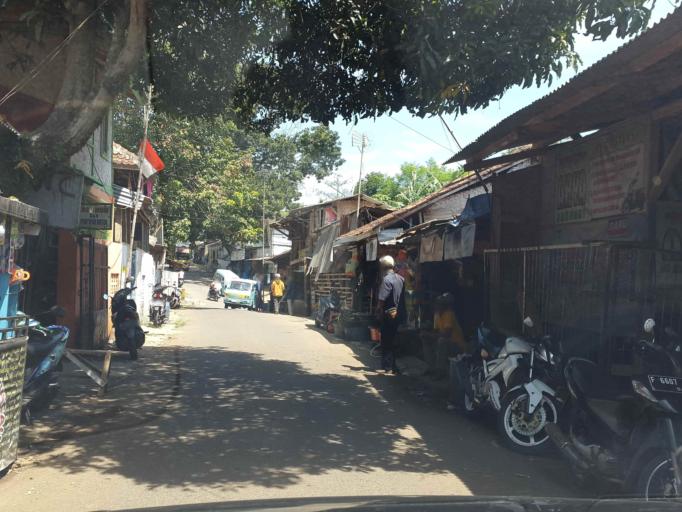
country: ID
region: West Java
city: Ciranjang-hilir
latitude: -6.7443
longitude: 107.2619
